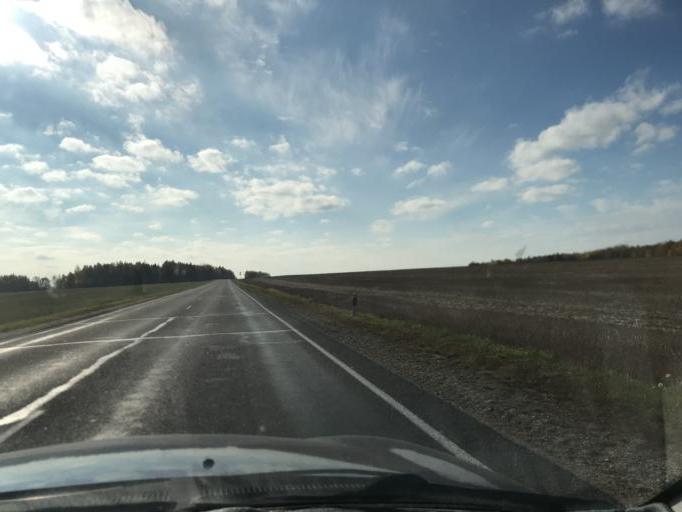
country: BY
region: Grodnenskaya
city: Voranava
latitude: 54.1953
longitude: 25.3458
